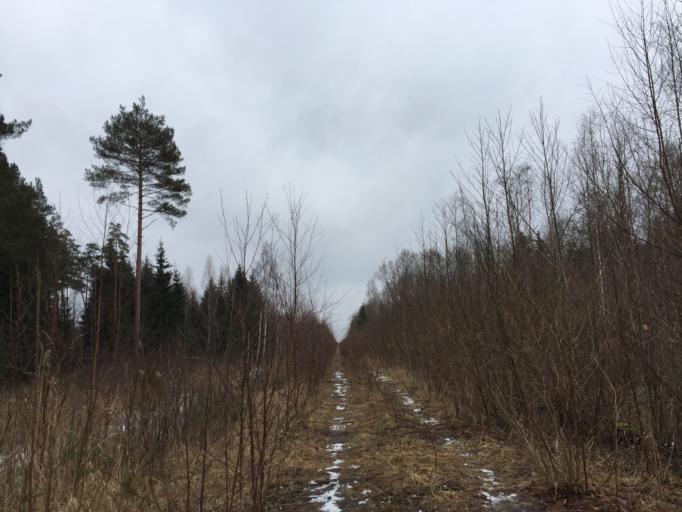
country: LV
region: Lielvarde
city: Lielvarde
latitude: 56.7619
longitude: 24.8187
